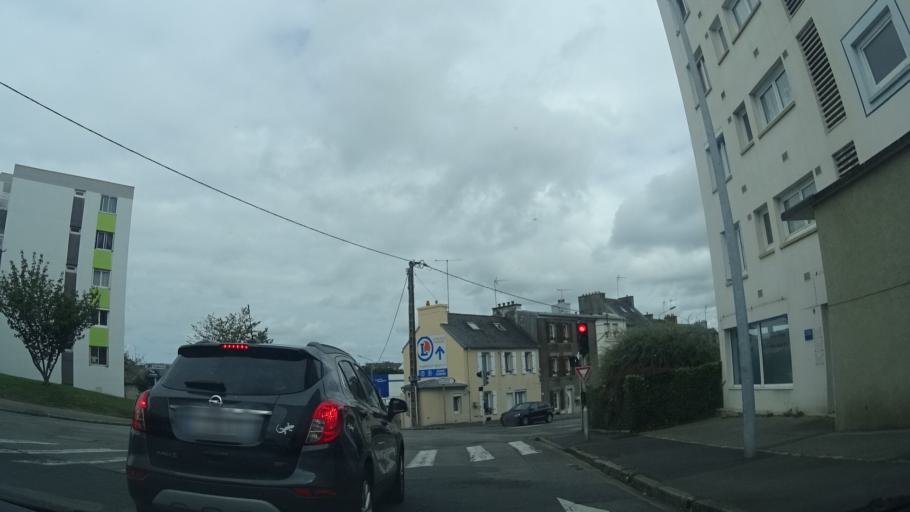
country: FR
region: Brittany
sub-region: Departement du Finistere
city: Brest
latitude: 48.4094
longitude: -4.4563
